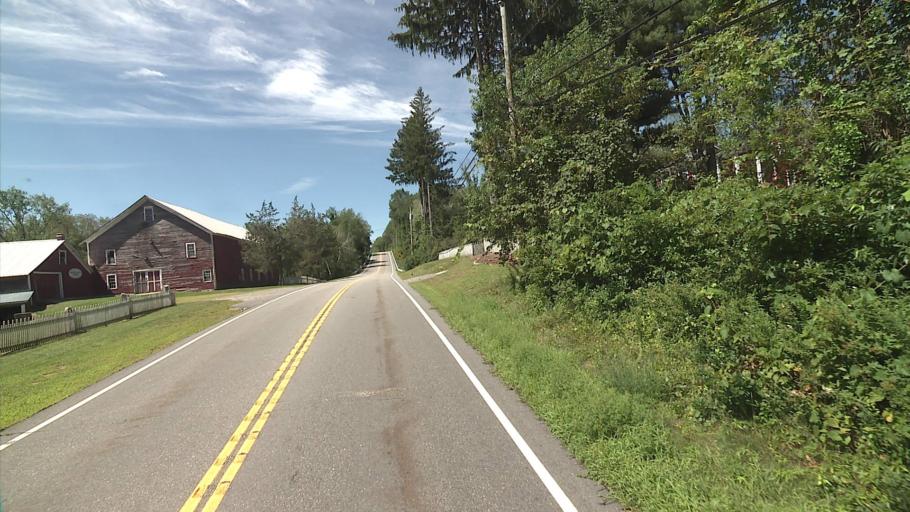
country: US
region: Connecticut
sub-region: Windham County
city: South Woodstock
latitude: 41.8972
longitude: -72.0304
